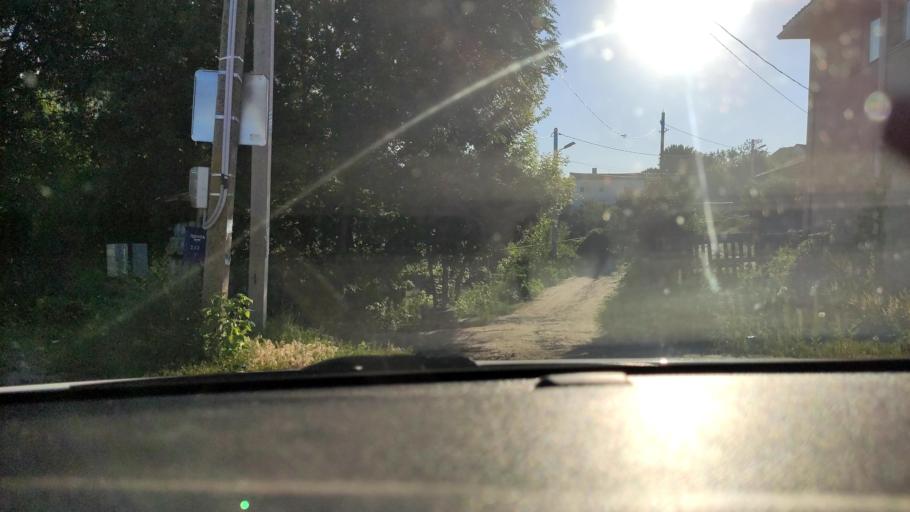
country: RU
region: Voronezj
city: Voronezh
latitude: 51.6262
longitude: 39.1977
